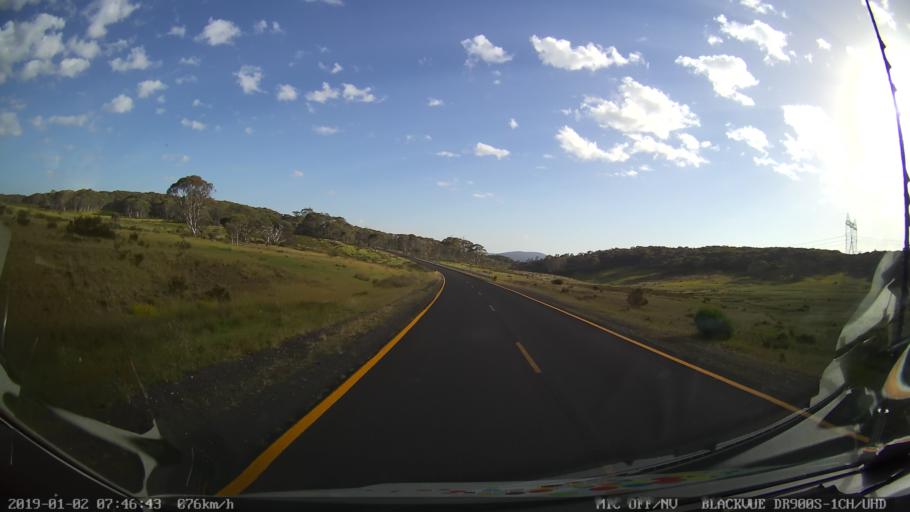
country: AU
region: New South Wales
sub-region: Tumut Shire
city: Tumut
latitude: -35.7724
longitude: 148.5195
